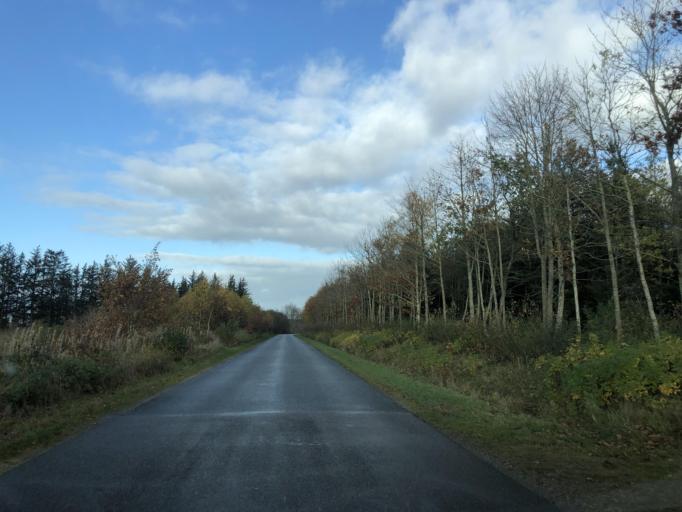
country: DK
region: Central Jutland
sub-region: Holstebro Kommune
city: Ulfborg
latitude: 56.1837
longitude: 8.4205
